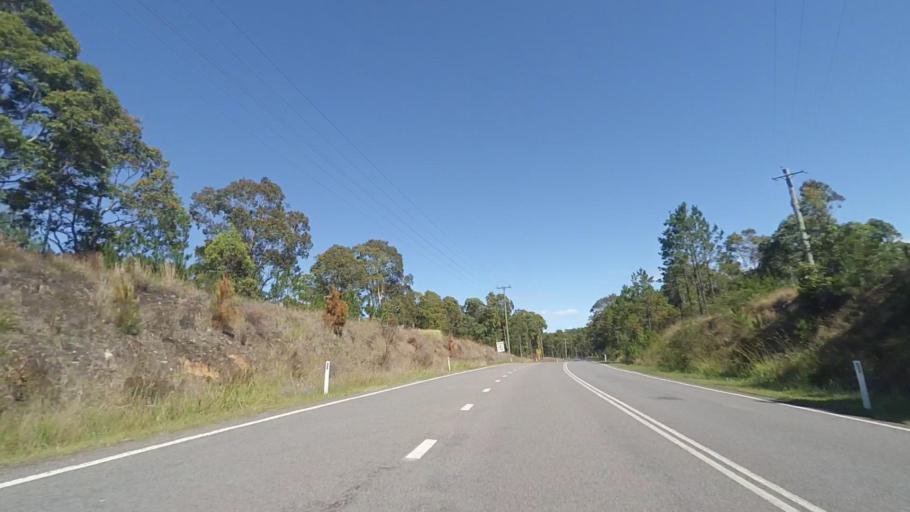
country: AU
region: New South Wales
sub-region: Great Lakes
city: Hawks Nest
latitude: -32.6187
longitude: 152.1126
